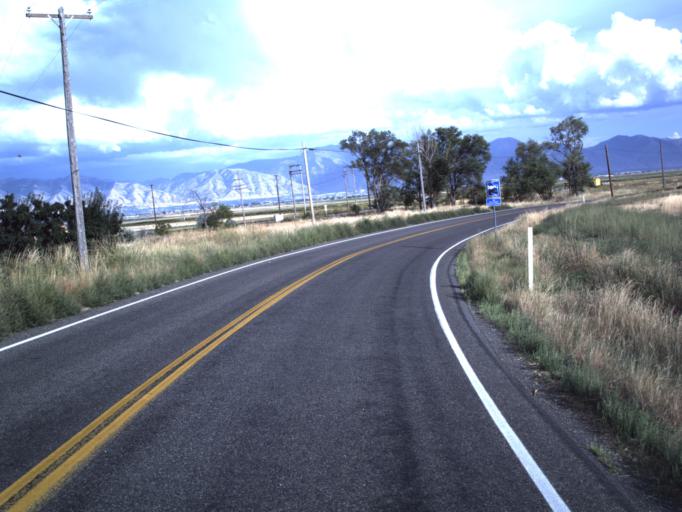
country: US
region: Utah
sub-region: Cache County
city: Benson
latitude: 41.8336
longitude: -112.0042
